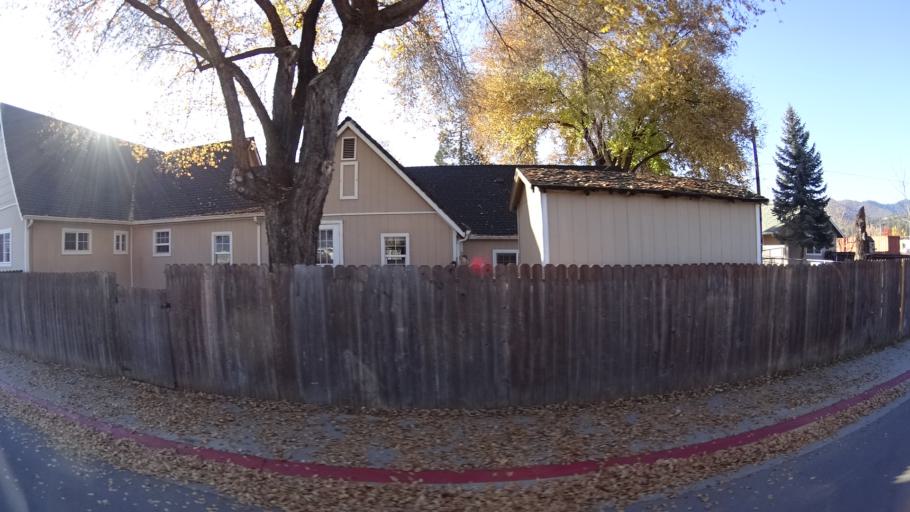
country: US
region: California
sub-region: Siskiyou County
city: Yreka
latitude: 41.7185
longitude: -122.6403
